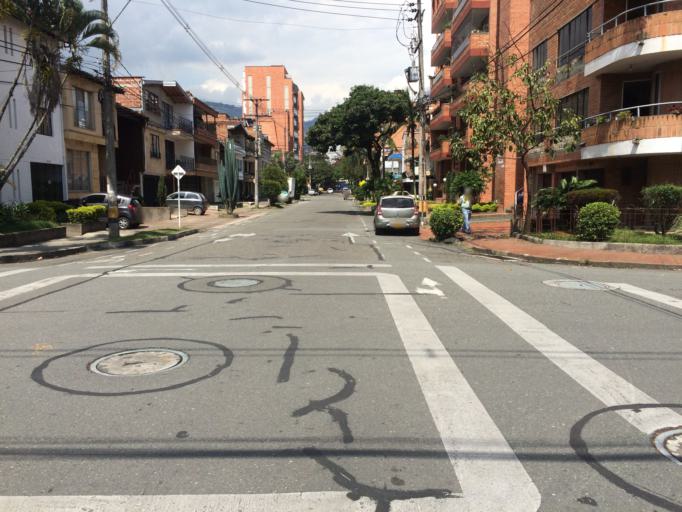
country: CO
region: Antioquia
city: Medellin
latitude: 6.2598
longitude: -75.5967
